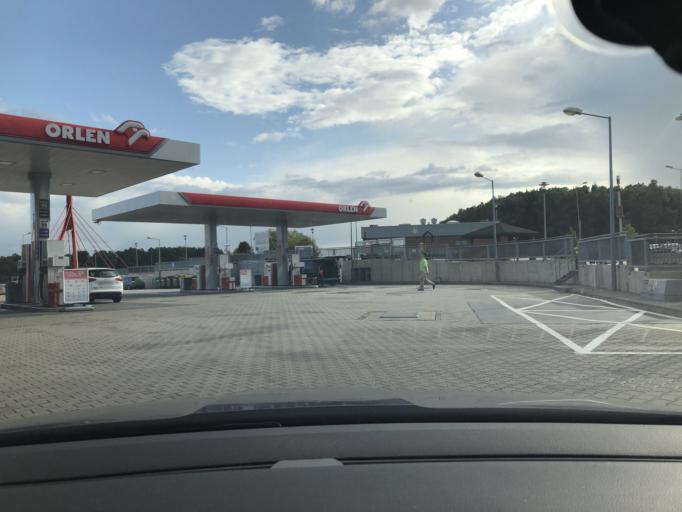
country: PL
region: Opole Voivodeship
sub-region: Powiat strzelecki
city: Lesnica
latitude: 50.4633
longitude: 18.1606
